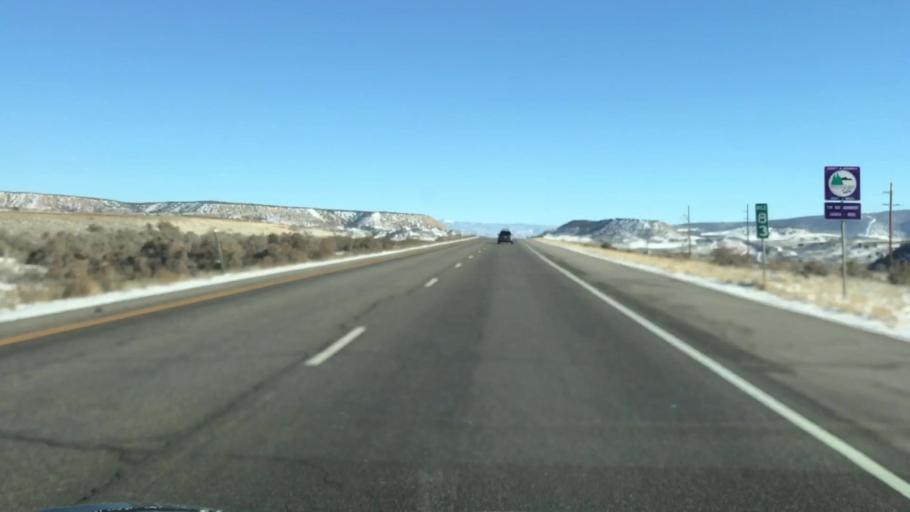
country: US
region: Colorado
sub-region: Garfield County
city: Battlement Mesa
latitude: 39.5000
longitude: -107.9111
